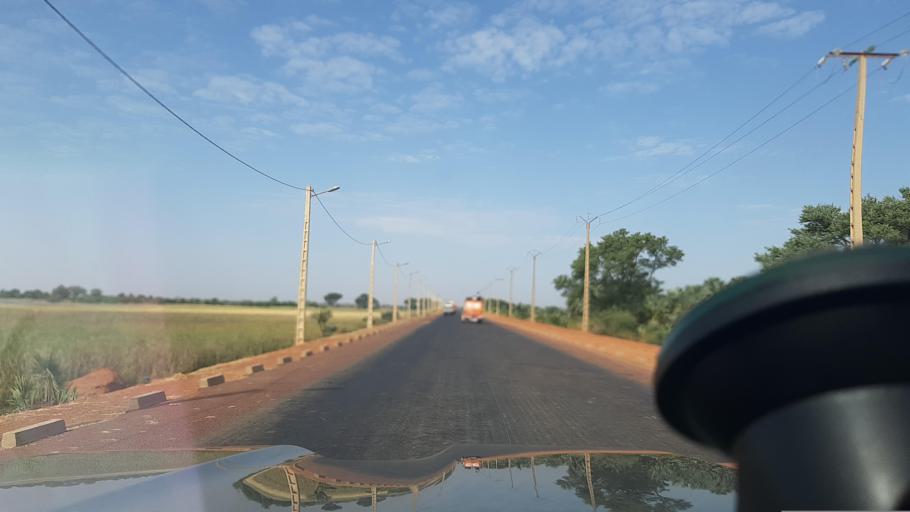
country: ML
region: Segou
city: Markala
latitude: 13.6836
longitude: -6.0922
